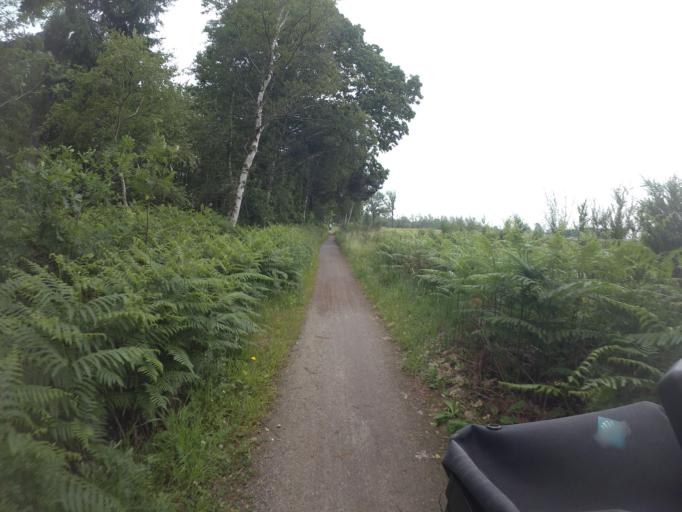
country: NL
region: Drenthe
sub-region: Gemeente Westerveld
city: Dwingeloo
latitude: 52.8141
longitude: 6.4138
